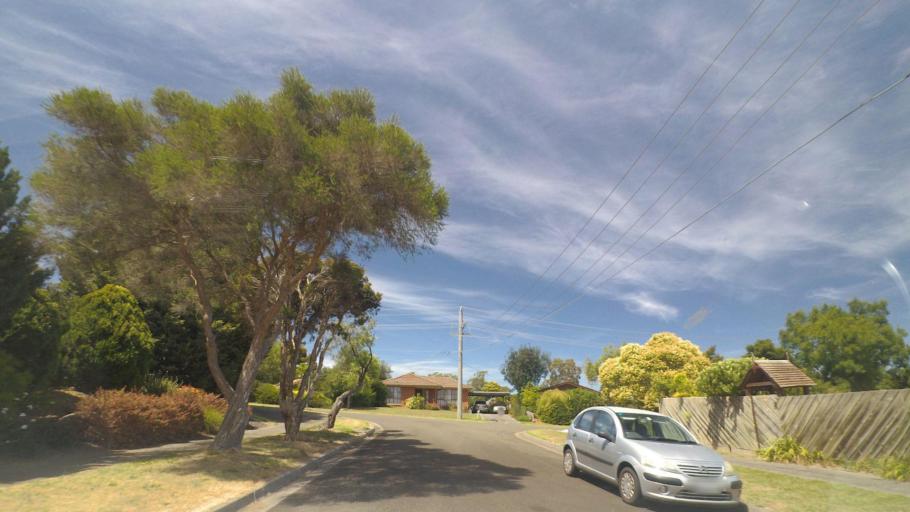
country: AU
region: Victoria
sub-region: Maroondah
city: Croydon North
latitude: -37.7711
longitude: 145.3062
